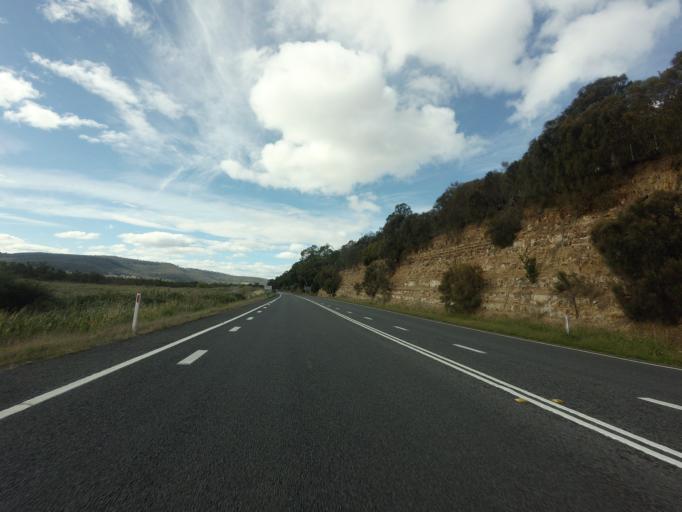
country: AU
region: Tasmania
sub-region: Glenorchy
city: Granton
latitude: -42.7505
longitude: 147.1738
